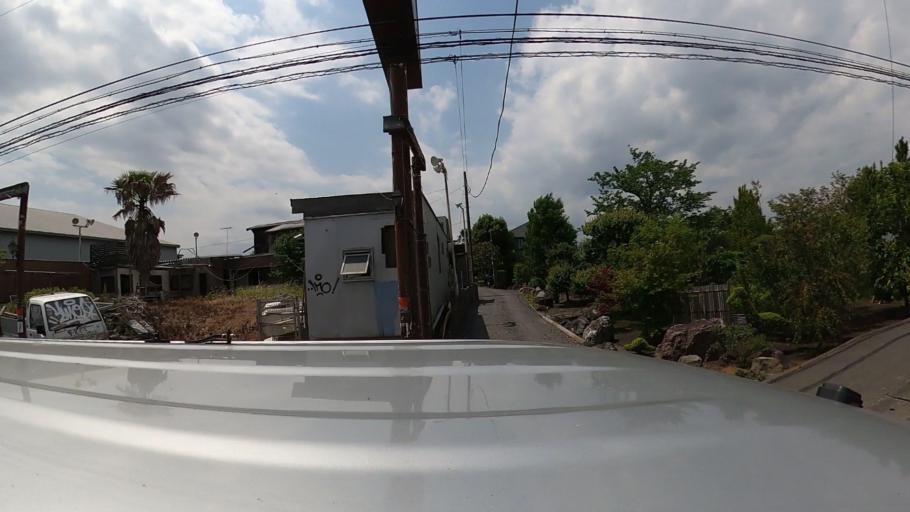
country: JP
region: Kanagawa
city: Chigasaki
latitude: 35.3874
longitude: 139.4022
